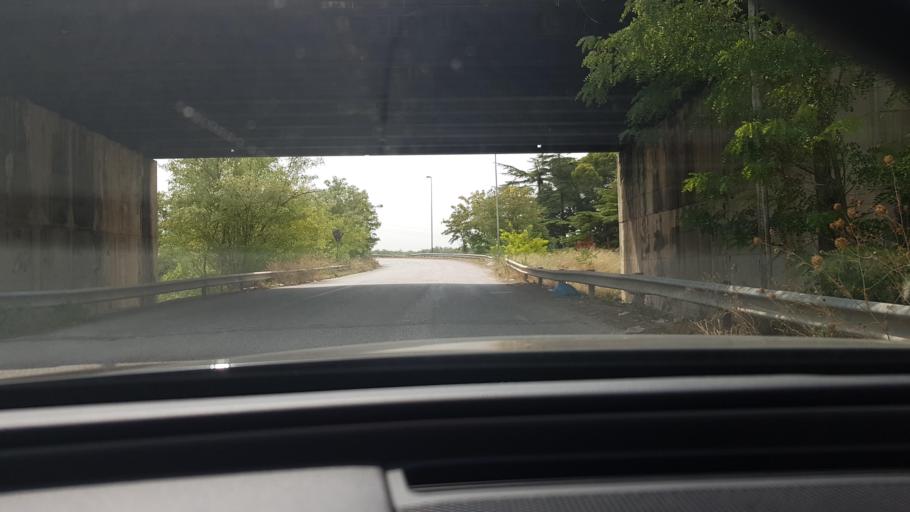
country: IT
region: Apulia
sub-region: Provincia di Barletta - Andria - Trani
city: Andria
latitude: 41.2153
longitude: 16.2651
